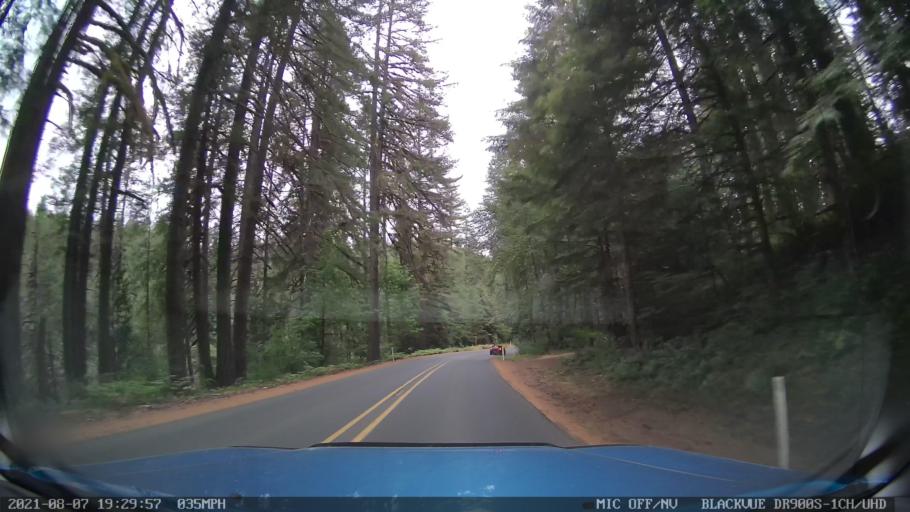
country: US
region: Oregon
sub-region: Linn County
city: Lyons
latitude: 44.8837
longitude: -122.6234
